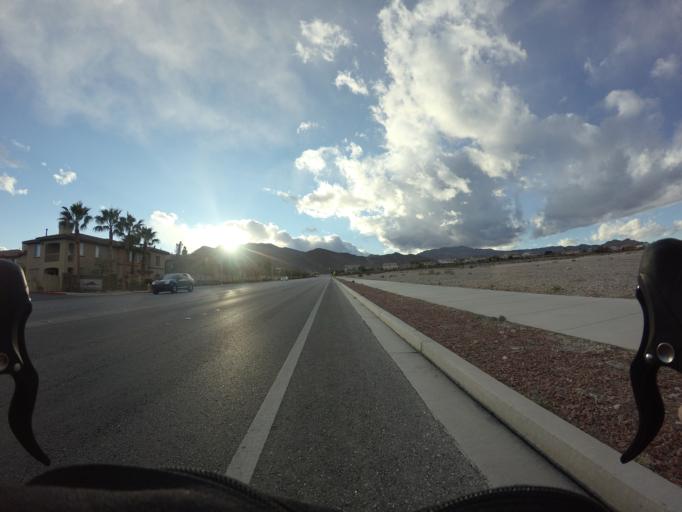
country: US
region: Nevada
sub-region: Clark County
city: Summerlin South
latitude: 36.2330
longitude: -115.3172
